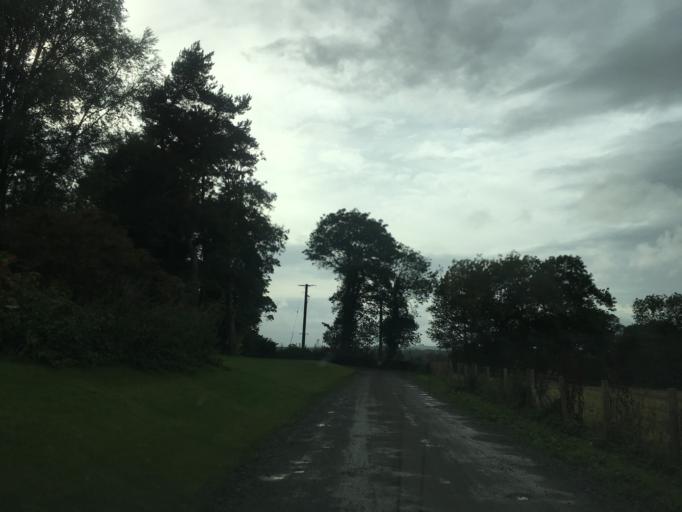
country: GB
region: Scotland
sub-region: West Lothian
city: Kirknewton
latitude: 55.9077
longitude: -3.4238
